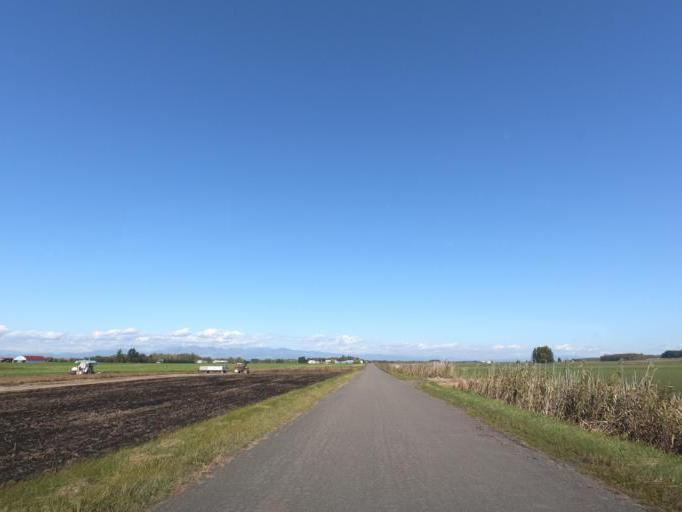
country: JP
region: Hokkaido
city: Otofuke
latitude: 43.0185
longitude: 143.2680
